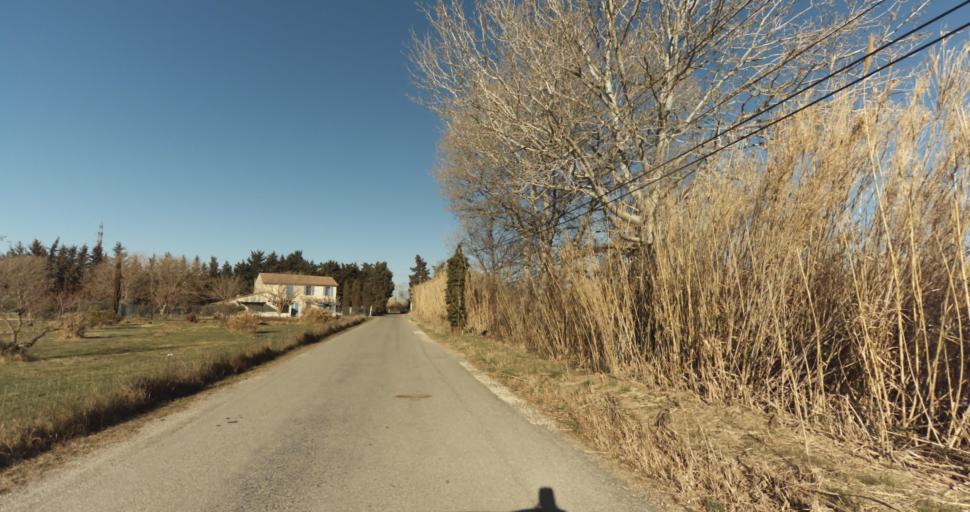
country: FR
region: Provence-Alpes-Cote d'Azur
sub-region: Departement des Bouches-du-Rhone
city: Rognonas
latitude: 43.9109
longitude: 4.7903
